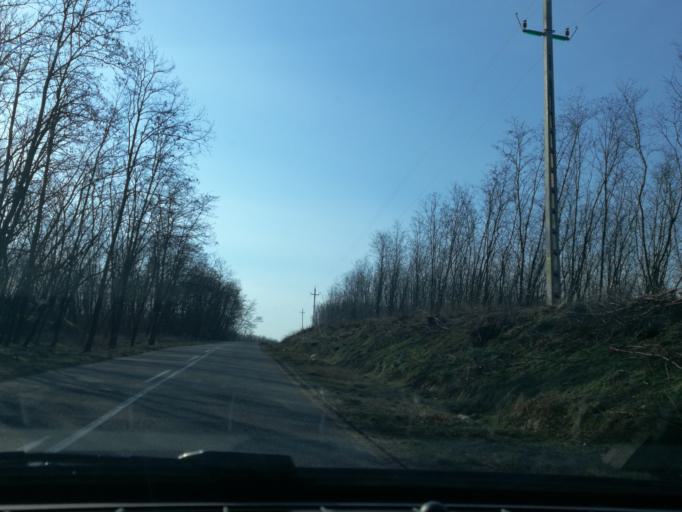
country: HU
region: Szabolcs-Szatmar-Bereg
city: Levelek
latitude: 47.9983
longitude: 21.9659
